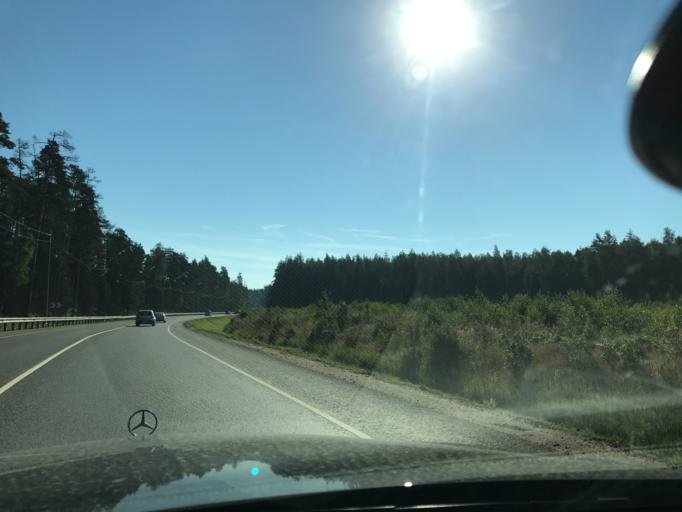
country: RU
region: Moskovskaya
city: Chernogolovka
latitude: 55.9808
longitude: 38.3140
